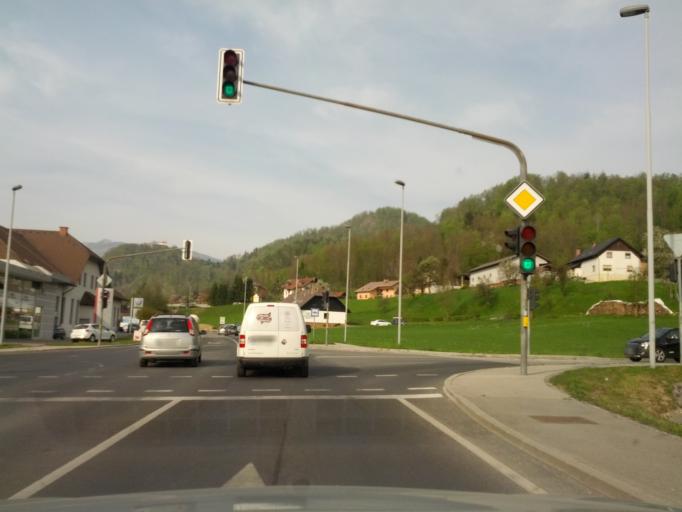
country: SI
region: Kamnik
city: Kamnik
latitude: 46.2094
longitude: 14.6071
